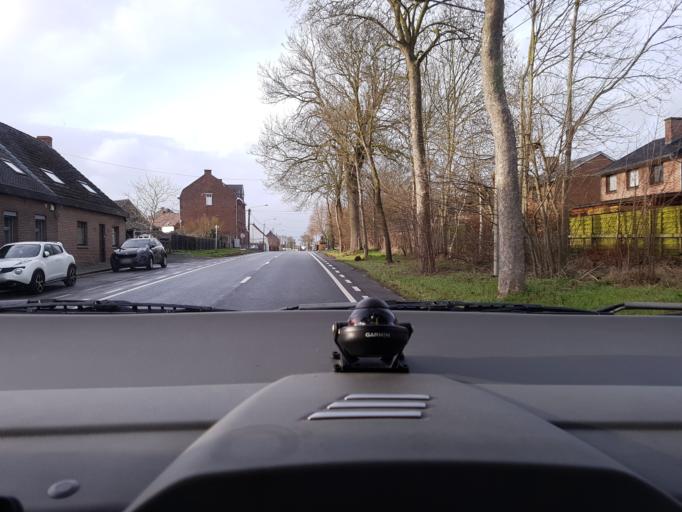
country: BE
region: Wallonia
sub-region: Province du Hainaut
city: Antoing
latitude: 50.5890
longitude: 3.5408
